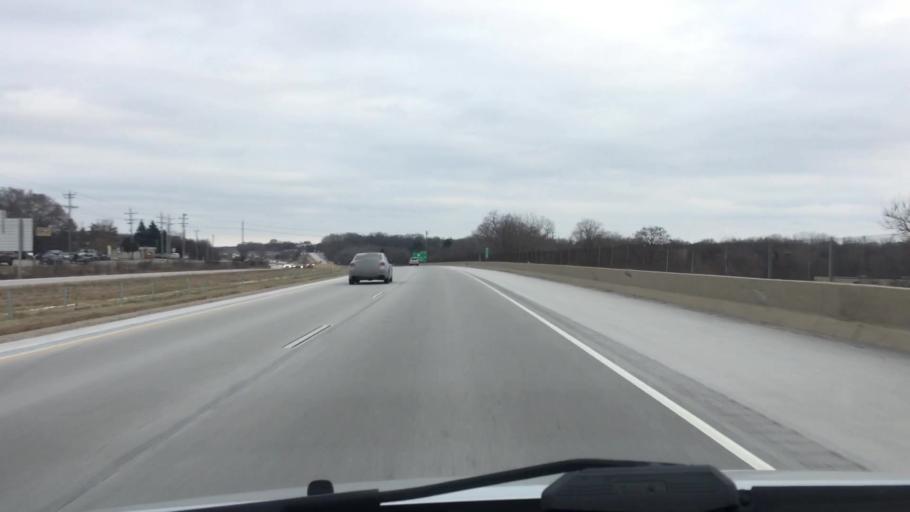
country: US
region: Wisconsin
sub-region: Waukesha County
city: Nashotah
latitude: 43.1021
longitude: -88.4164
